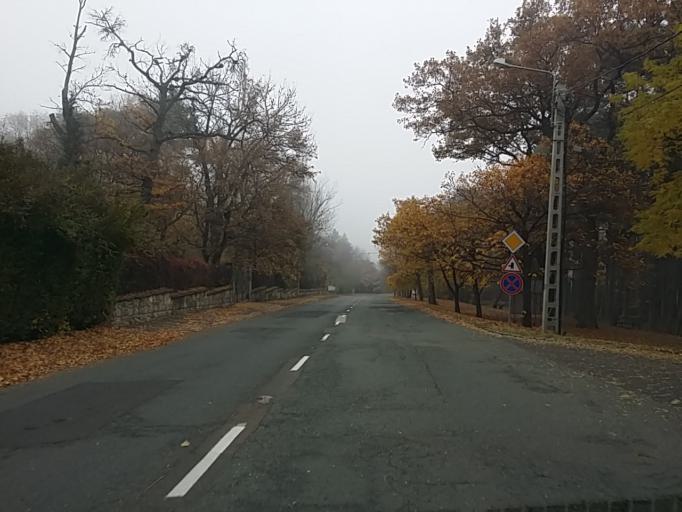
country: HU
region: Heves
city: Gyongyossolymos
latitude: 47.8332
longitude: 19.9677
